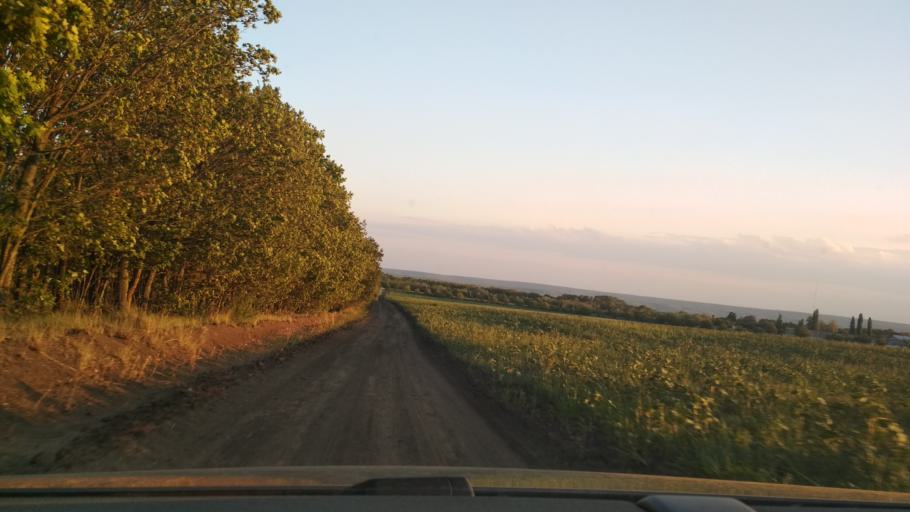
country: MD
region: Straseni
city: Straseni
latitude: 47.1853
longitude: 28.6514
